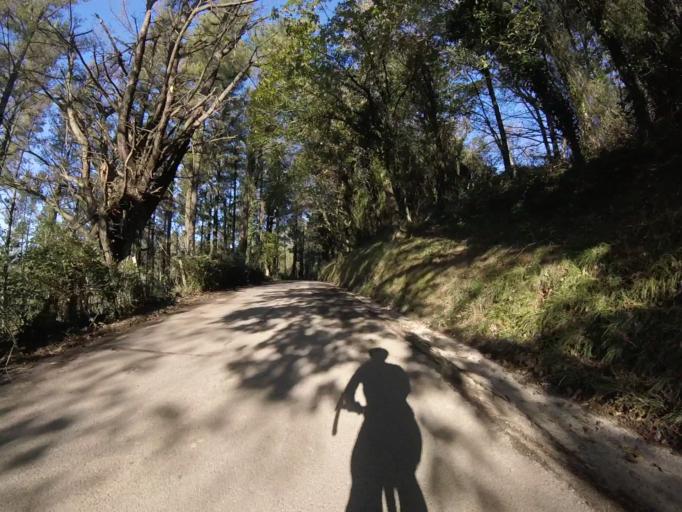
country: ES
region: Basque Country
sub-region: Provincia de Guipuzcoa
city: Usurbil
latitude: 43.2860
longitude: -2.0703
